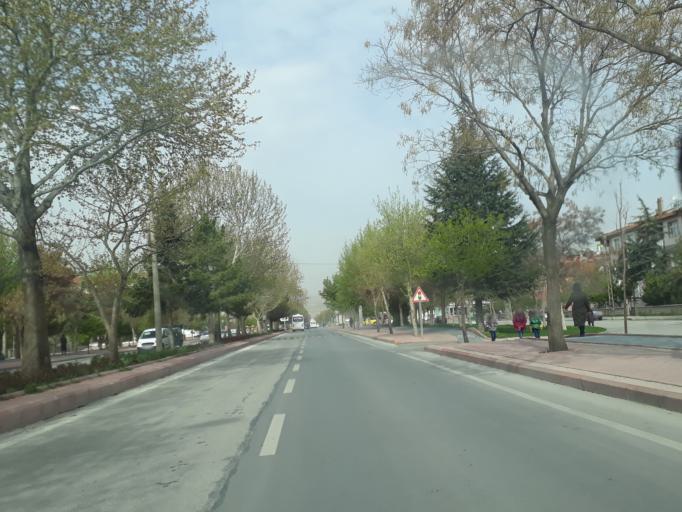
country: TR
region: Konya
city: Selcuklu
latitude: 37.9372
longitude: 32.5053
